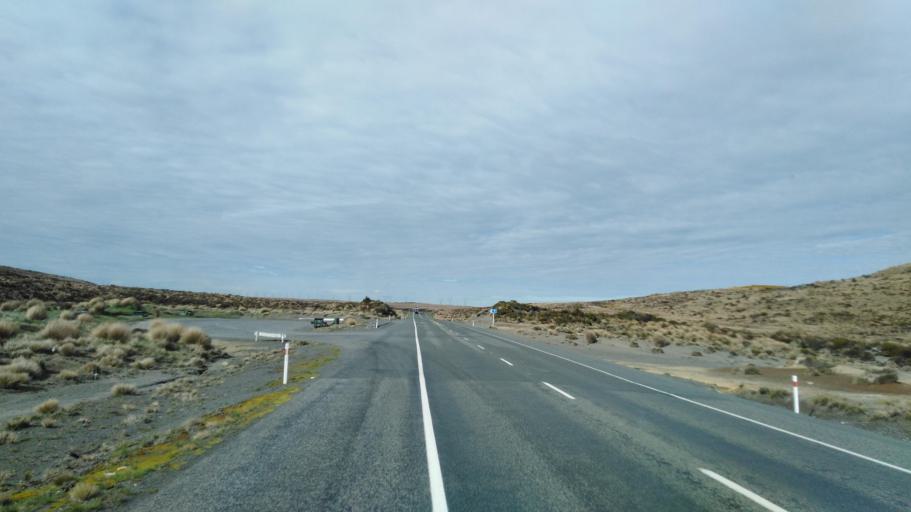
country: NZ
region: Manawatu-Wanganui
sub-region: Ruapehu District
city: Waiouru
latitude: -39.3090
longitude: 175.7373
